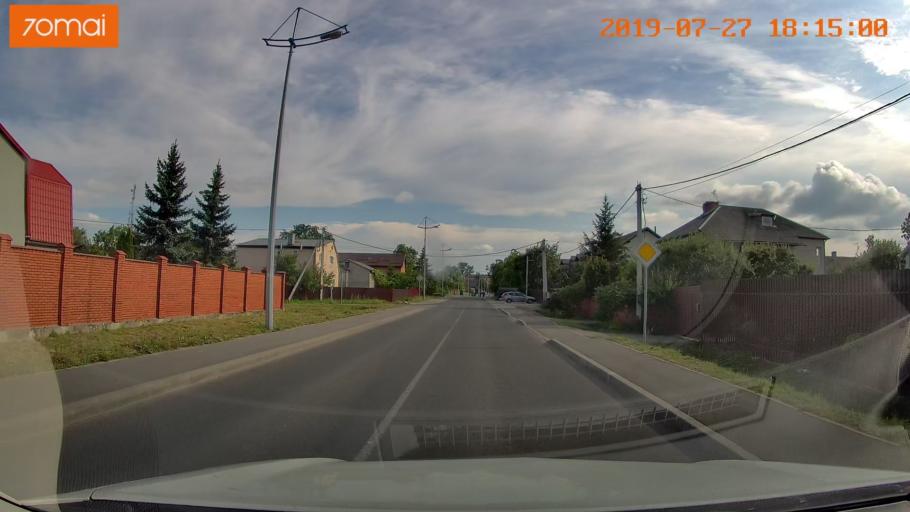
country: RU
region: Kaliningrad
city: Bol'shoe Isakovo
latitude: 54.7225
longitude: 20.6006
